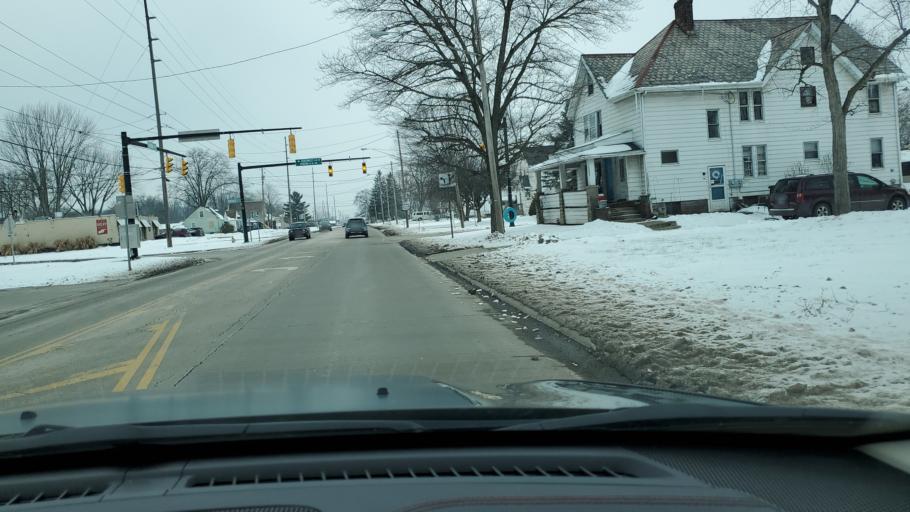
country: US
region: Ohio
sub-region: Trumbull County
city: Warren
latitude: 41.2462
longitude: -80.8455
